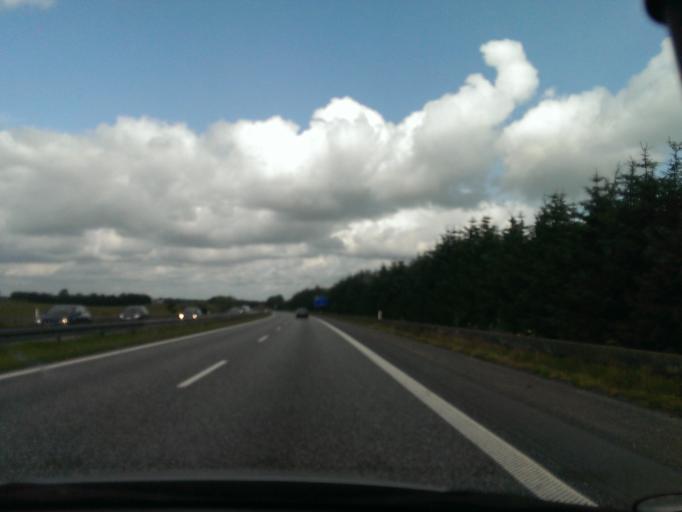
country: DK
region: Central Jutland
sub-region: Randers Kommune
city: Spentrup
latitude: 56.5375
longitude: 9.9182
